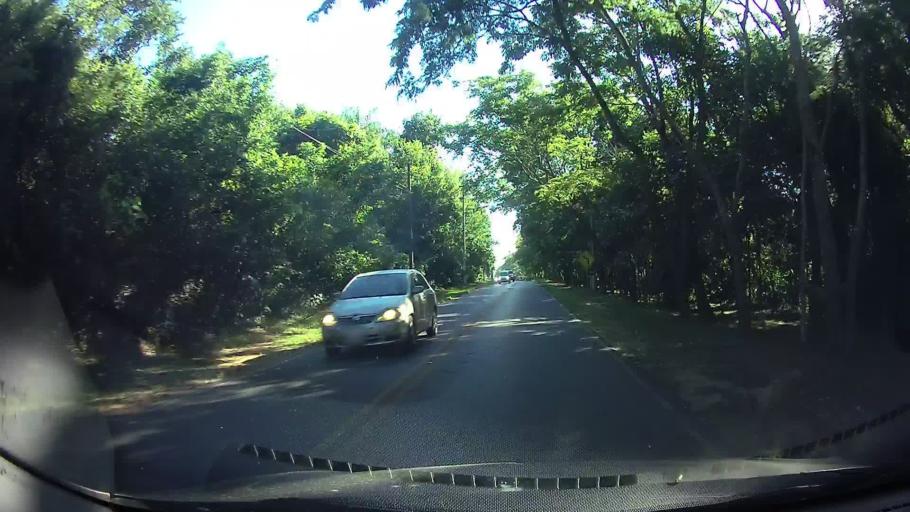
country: PY
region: Cordillera
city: Atyra
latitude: -25.2897
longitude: -57.1803
